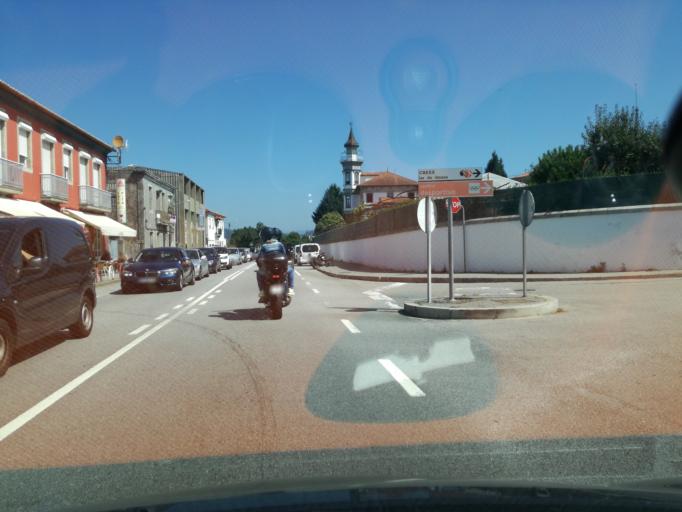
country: ES
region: Galicia
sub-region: Provincia de Pontevedra
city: O Rosal
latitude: 41.8966
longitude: -8.8187
